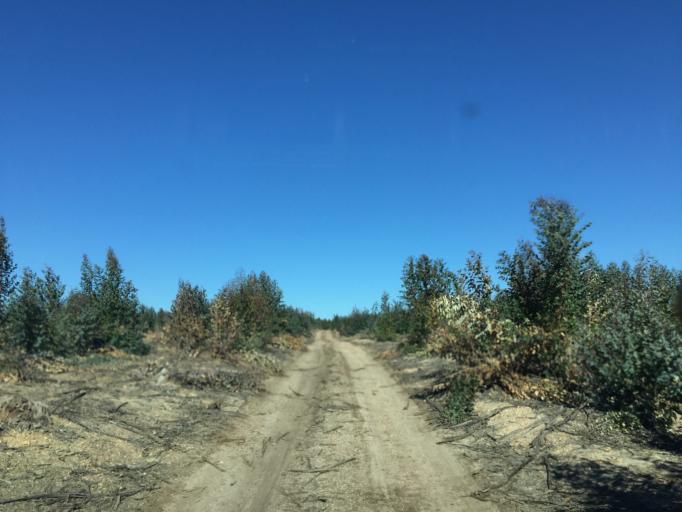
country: PT
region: Portalegre
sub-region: Nisa
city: Nisa
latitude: 39.4924
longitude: -7.7722
